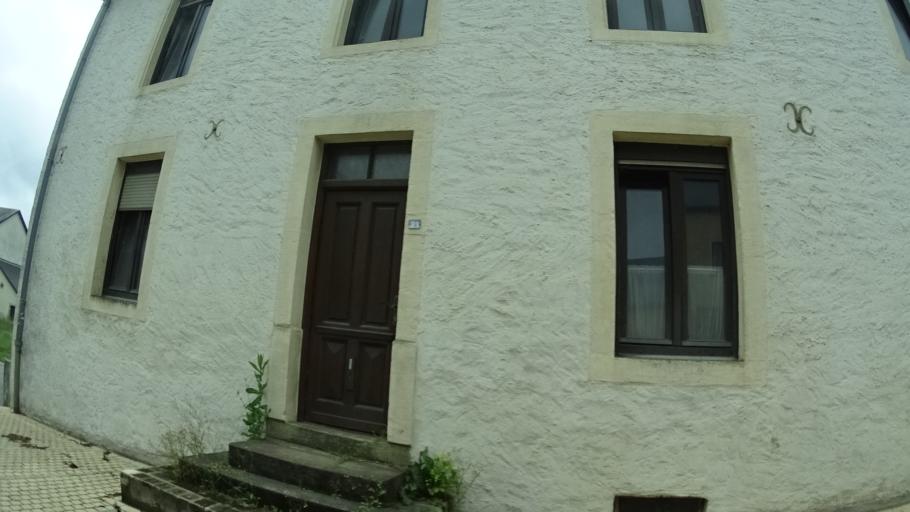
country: LU
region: Luxembourg
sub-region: Canton de Capellen
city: Steinfort
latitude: 49.6460
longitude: 5.9117
